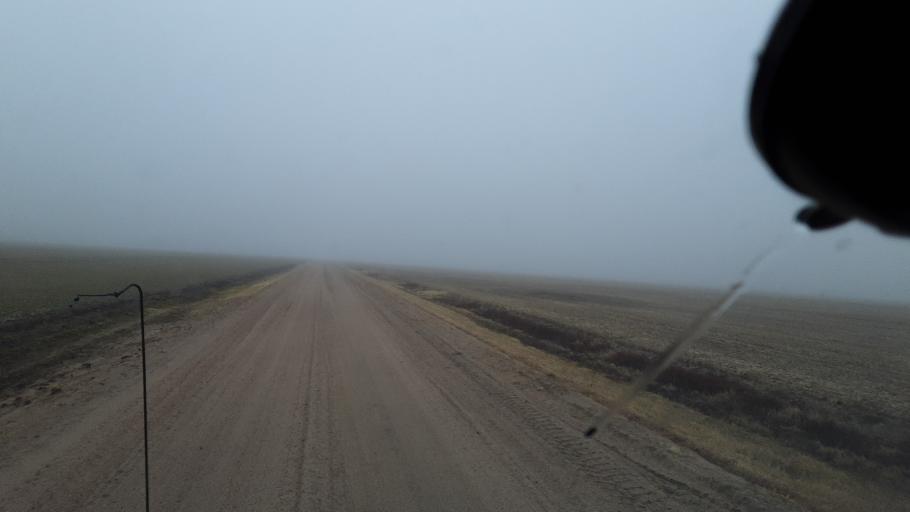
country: US
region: Kansas
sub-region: Reno County
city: South Hutchinson
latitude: 37.9677
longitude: -97.9956
